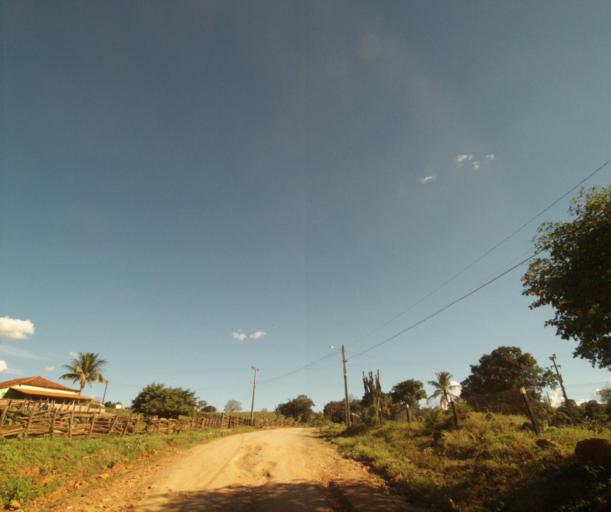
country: BR
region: Bahia
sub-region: Carinhanha
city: Carinhanha
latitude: -14.2664
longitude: -44.5250
